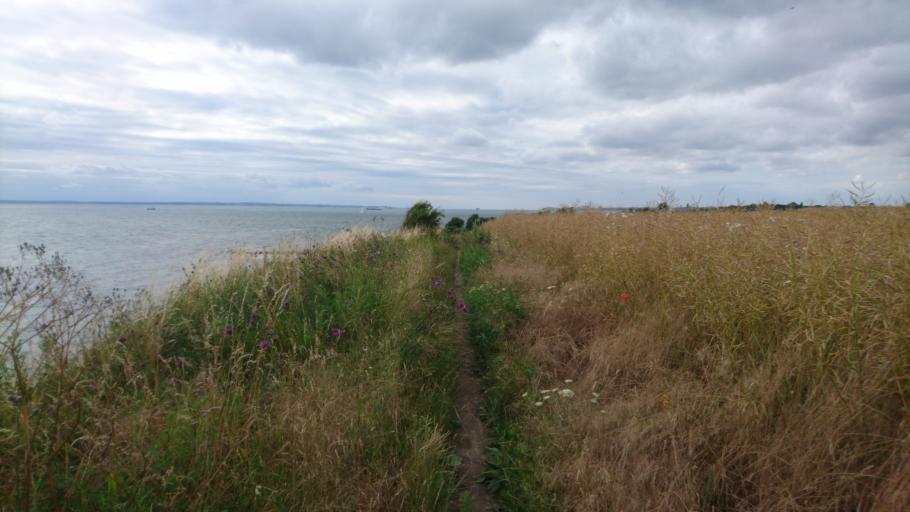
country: SE
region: Skane
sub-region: Helsingborg
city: Rydeback
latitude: 55.9509
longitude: 12.7621
